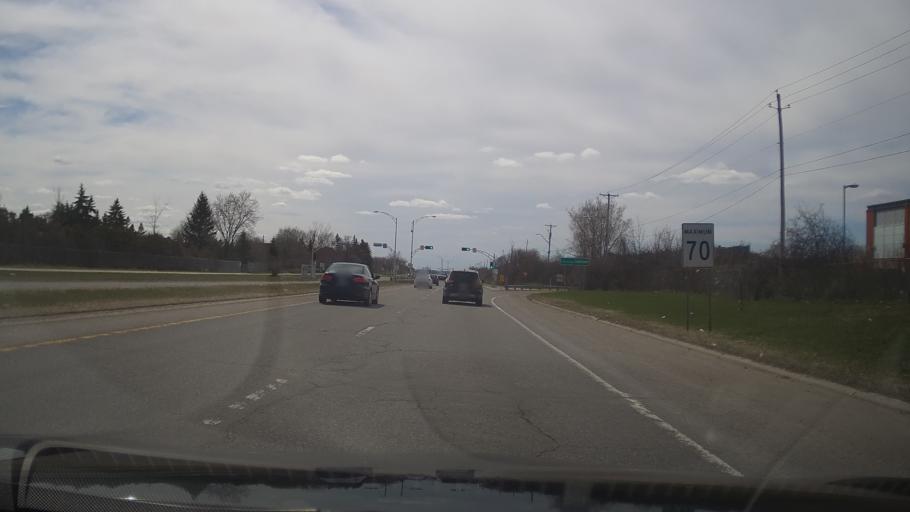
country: CA
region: Ontario
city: Bells Corners
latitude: 45.4104
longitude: -75.8411
